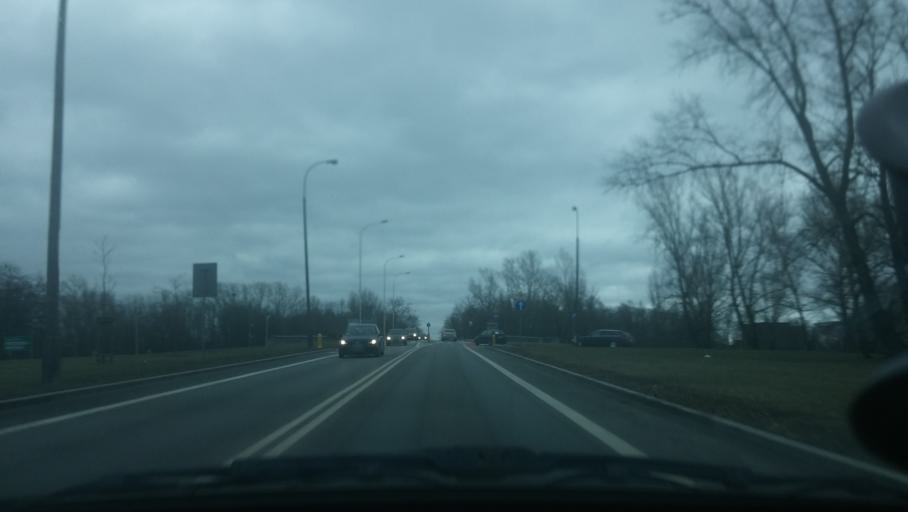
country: PL
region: Masovian Voivodeship
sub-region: Warszawa
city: Bialoleka
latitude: 52.3149
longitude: 21.0006
